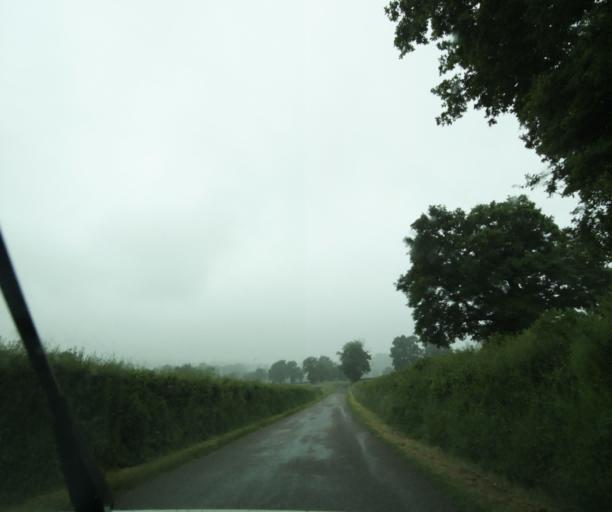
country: FR
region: Bourgogne
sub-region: Departement de Saone-et-Loire
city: Charolles
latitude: 46.4106
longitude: 4.2855
